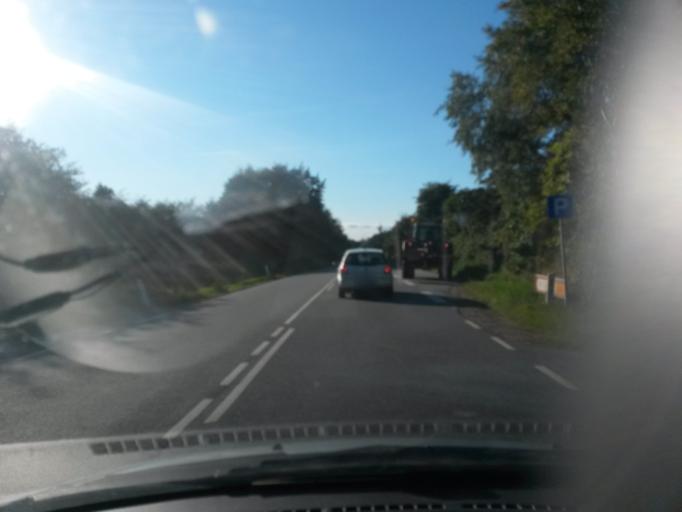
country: DK
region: Central Jutland
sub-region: Favrskov Kommune
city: Hammel
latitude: 56.2421
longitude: 9.7967
